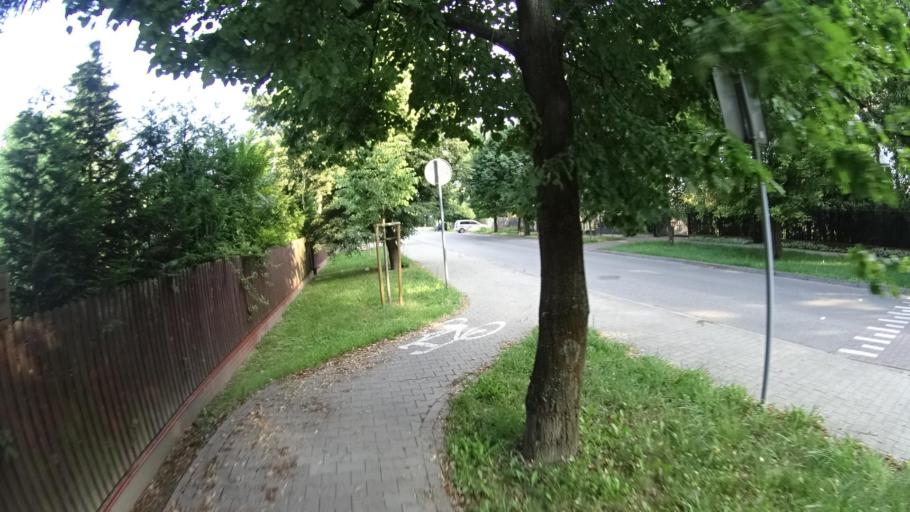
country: PL
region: Masovian Voivodeship
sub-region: Powiat pruszkowski
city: Michalowice
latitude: 52.1714
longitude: 20.8854
